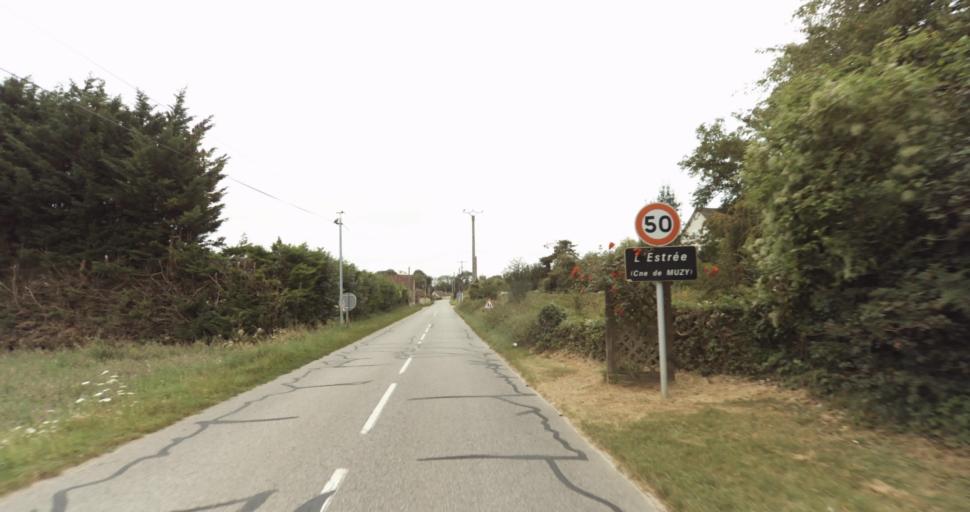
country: FR
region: Centre
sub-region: Departement d'Eure-et-Loir
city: Vert-en-Drouais
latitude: 48.7648
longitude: 1.3217
